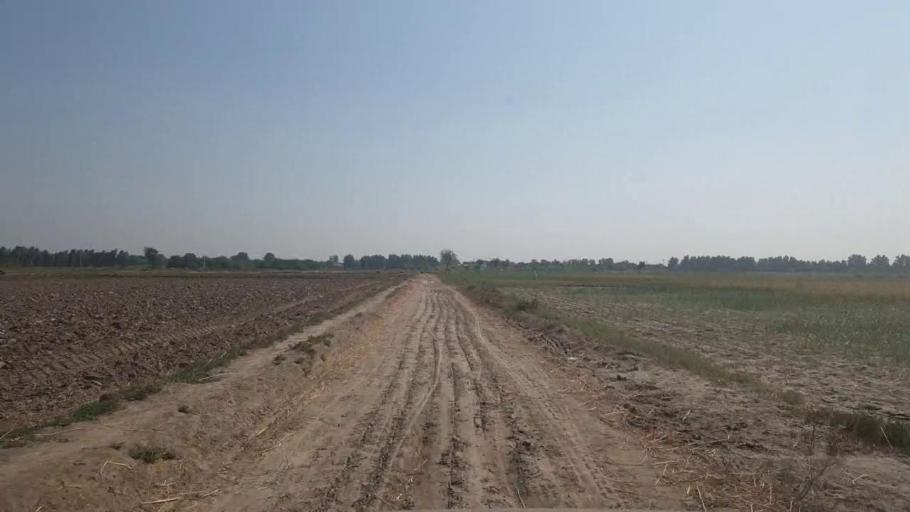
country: PK
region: Sindh
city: Badin
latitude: 24.6803
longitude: 68.8974
